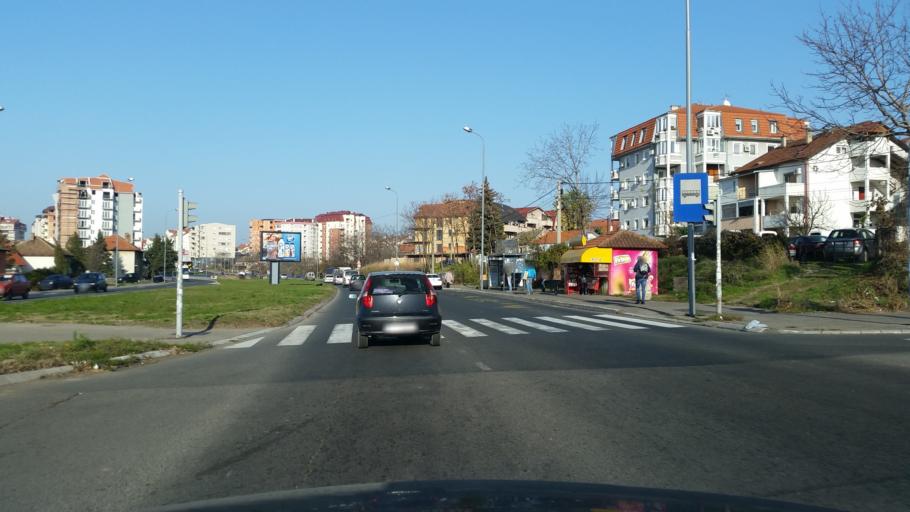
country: RS
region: Central Serbia
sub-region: Belgrade
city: Cukarica
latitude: 44.7543
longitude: 20.4144
